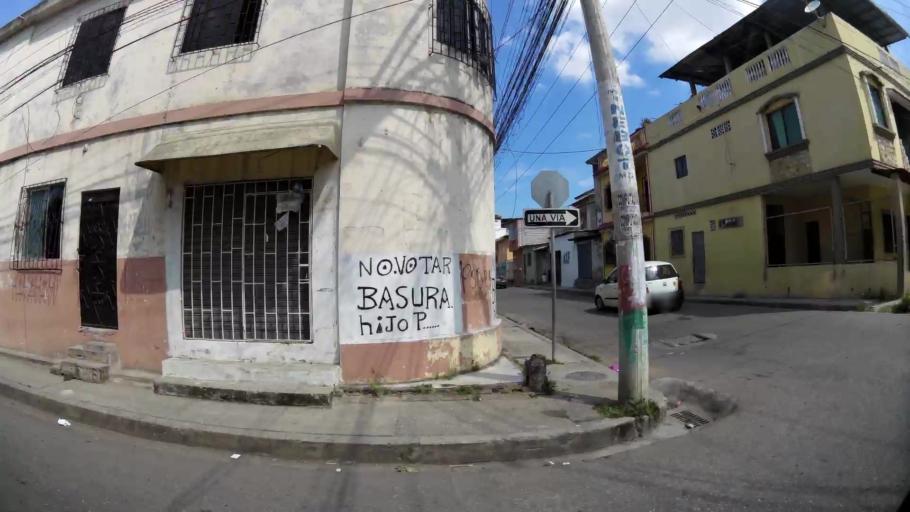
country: EC
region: Guayas
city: Guayaquil
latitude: -2.1340
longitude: -79.9375
